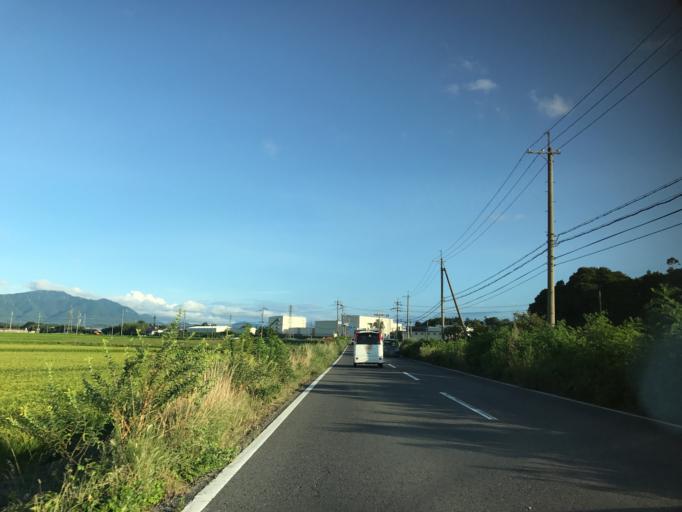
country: JP
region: Shiga Prefecture
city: Youkaichi
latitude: 35.0947
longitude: 136.2489
